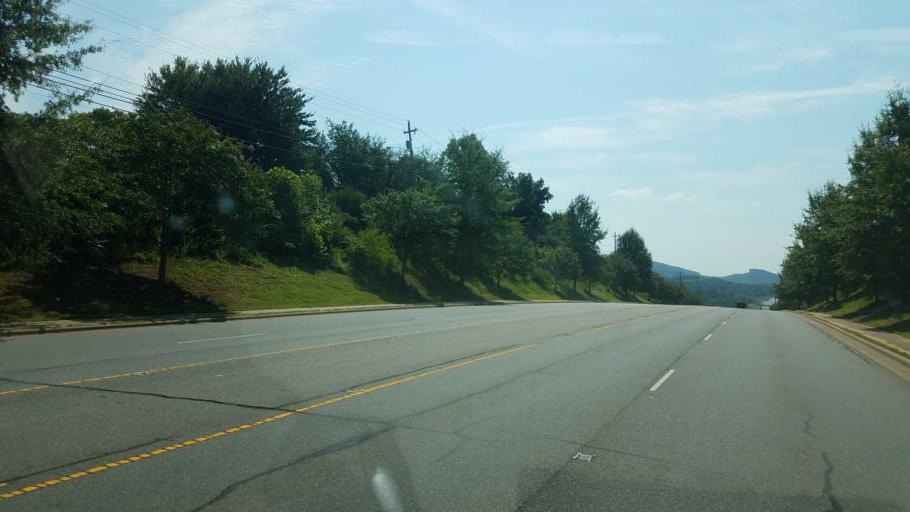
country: US
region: North Carolina
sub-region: Burke County
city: Morganton
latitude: 35.7295
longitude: -81.6685
